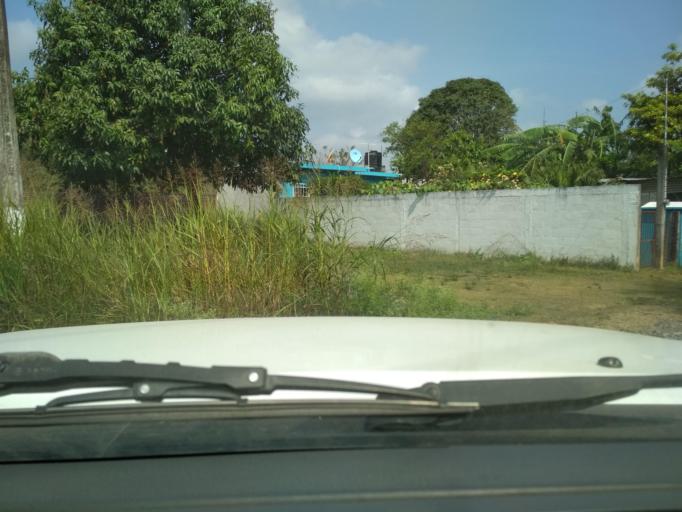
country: MX
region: Veracruz
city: El Tejar
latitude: 19.0773
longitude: -96.1648
